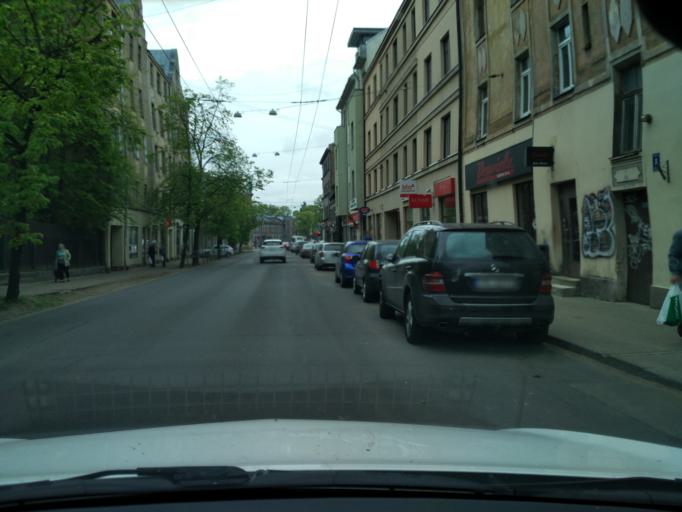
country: LV
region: Marupe
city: Marupe
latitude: 56.9342
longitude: 24.0713
